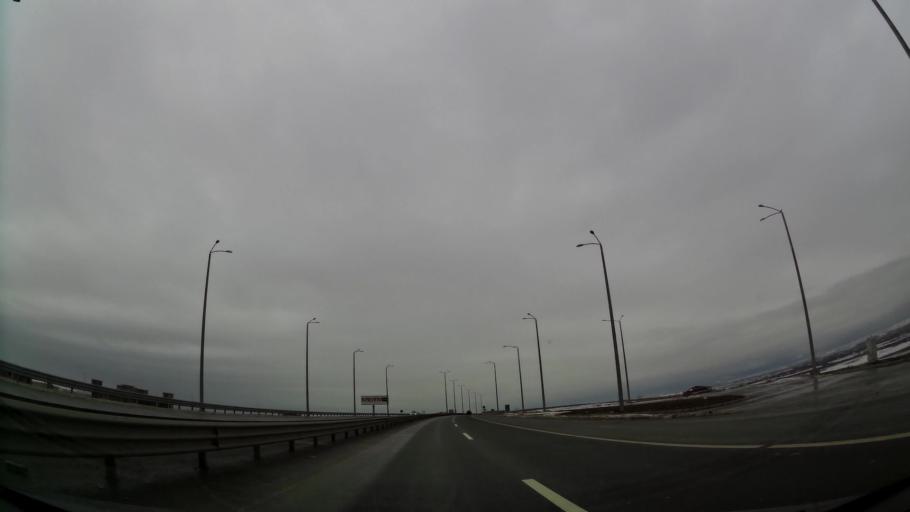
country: XK
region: Pristina
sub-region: Kosovo Polje
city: Kosovo Polje
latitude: 42.6282
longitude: 21.1342
